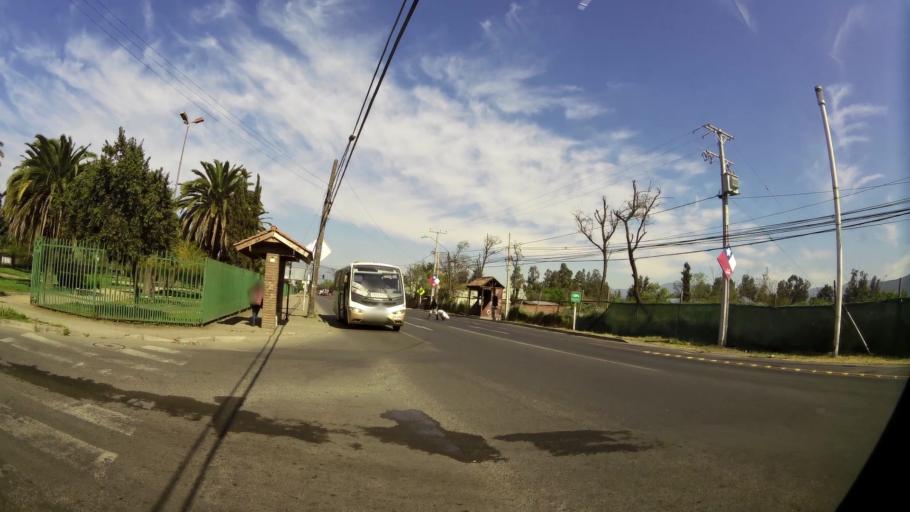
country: CL
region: Santiago Metropolitan
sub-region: Provincia de Talagante
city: Talagante
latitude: -33.6728
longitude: -70.9467
